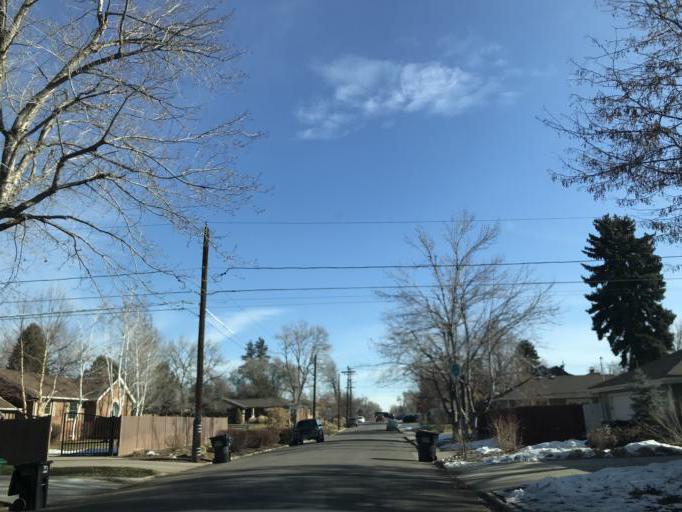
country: US
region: Colorado
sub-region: Arapahoe County
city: Glendale
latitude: 39.7356
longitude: -104.9055
